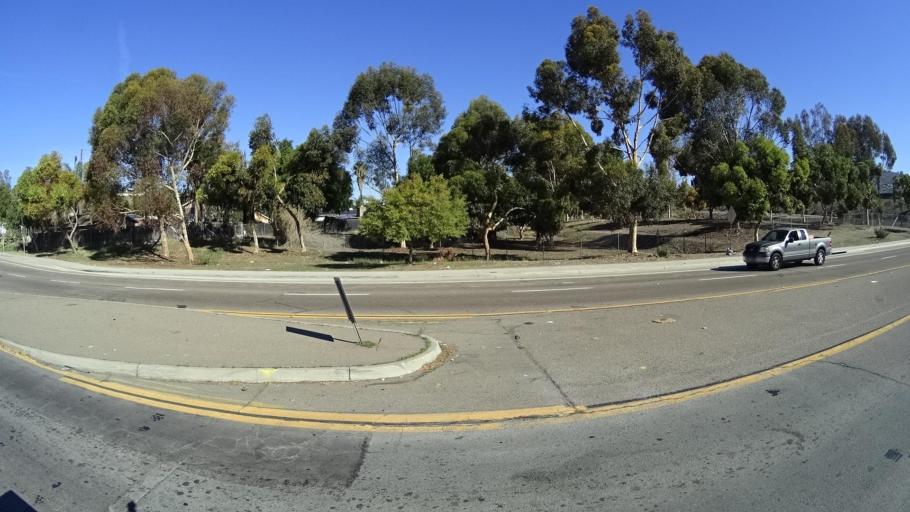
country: US
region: California
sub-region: San Diego County
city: La Presa
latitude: 32.7148
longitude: -117.0167
